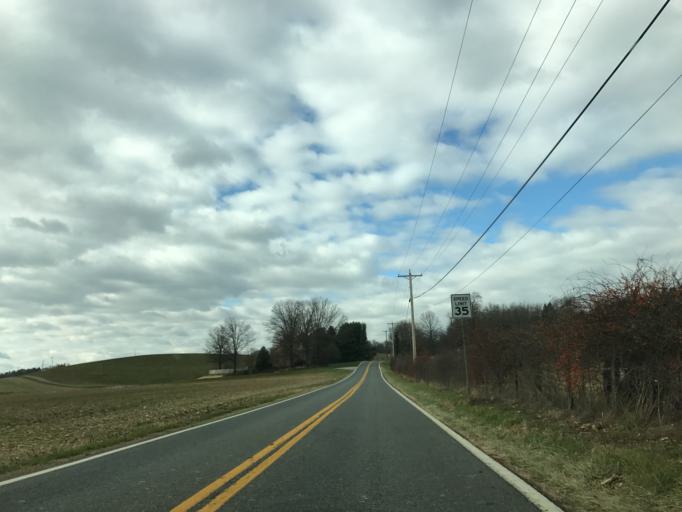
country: US
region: Maryland
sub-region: Baltimore County
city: Perry Hall
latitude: 39.4859
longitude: -76.4976
